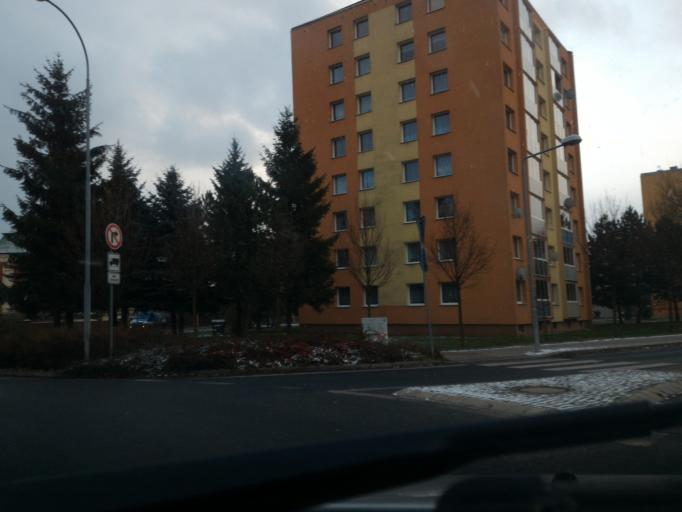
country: CZ
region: Ustecky
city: Varnsdorf
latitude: 50.9082
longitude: 14.6182
